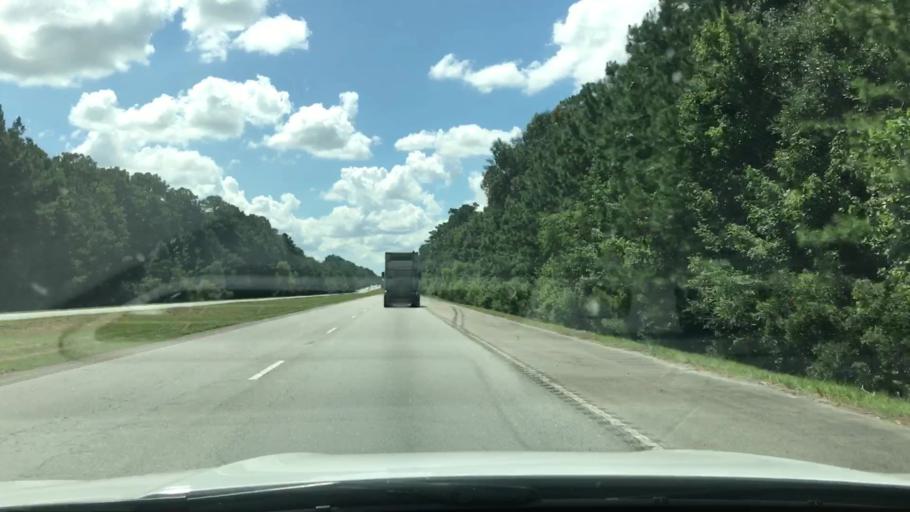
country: US
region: South Carolina
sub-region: Berkeley County
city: Hanahan
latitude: 32.9423
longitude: -79.9986
